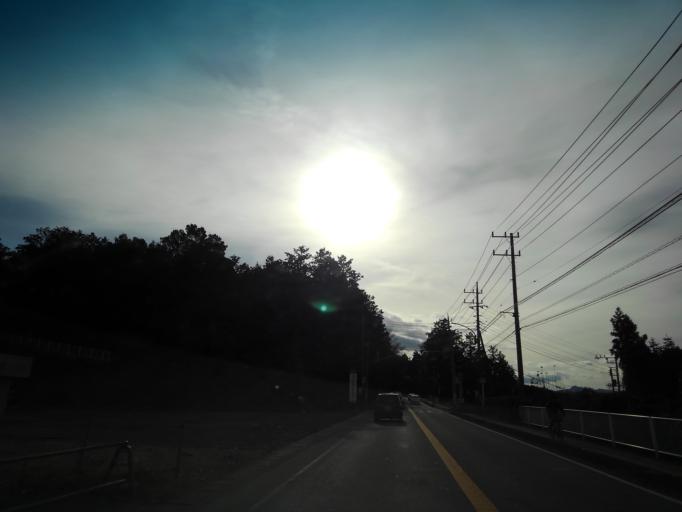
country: JP
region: Saitama
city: Hanno
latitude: 35.8770
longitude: 139.3353
